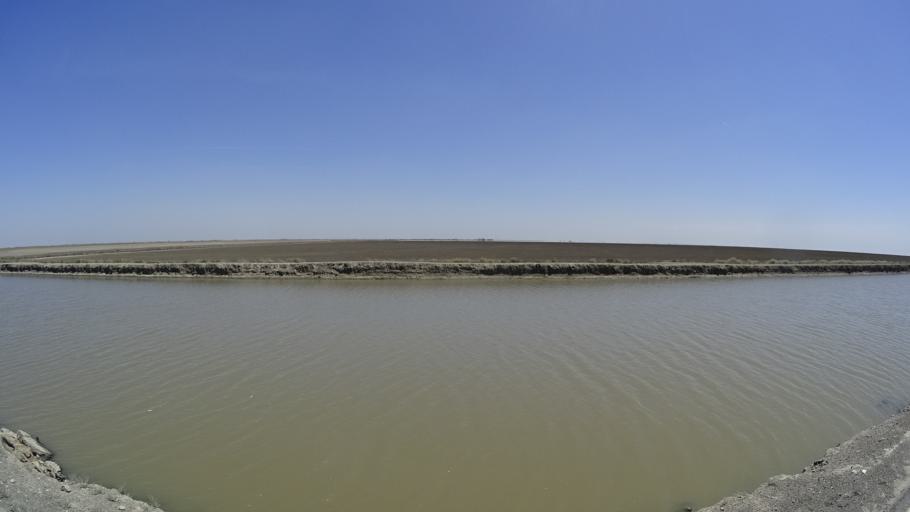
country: US
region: California
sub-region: Kings County
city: Corcoran
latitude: 36.0405
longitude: -119.6434
